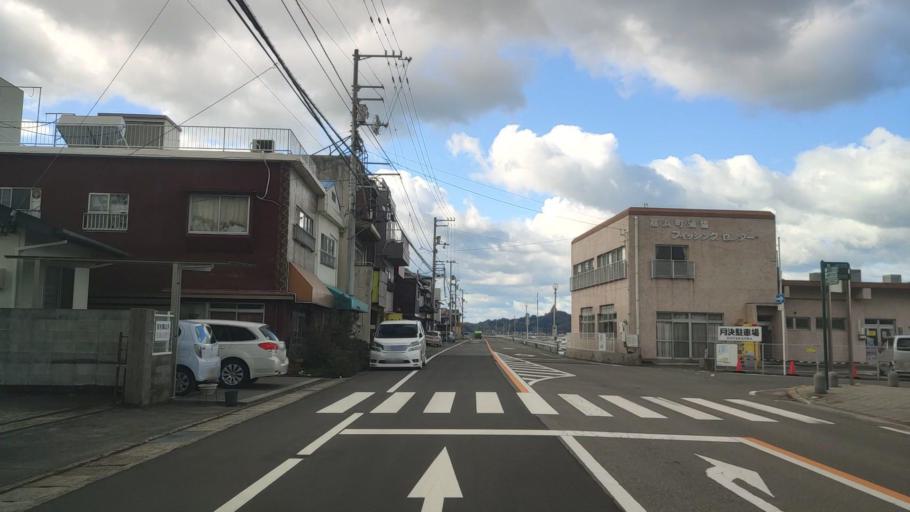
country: JP
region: Ehime
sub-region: Shikoku-chuo Shi
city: Matsuyama
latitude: 33.8877
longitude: 132.7031
